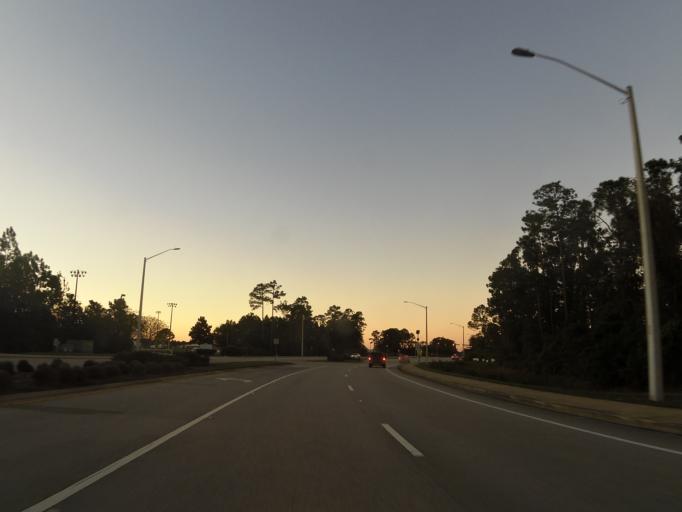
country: US
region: Florida
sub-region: Flagler County
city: Palm Coast
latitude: 29.5749
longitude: -81.2543
